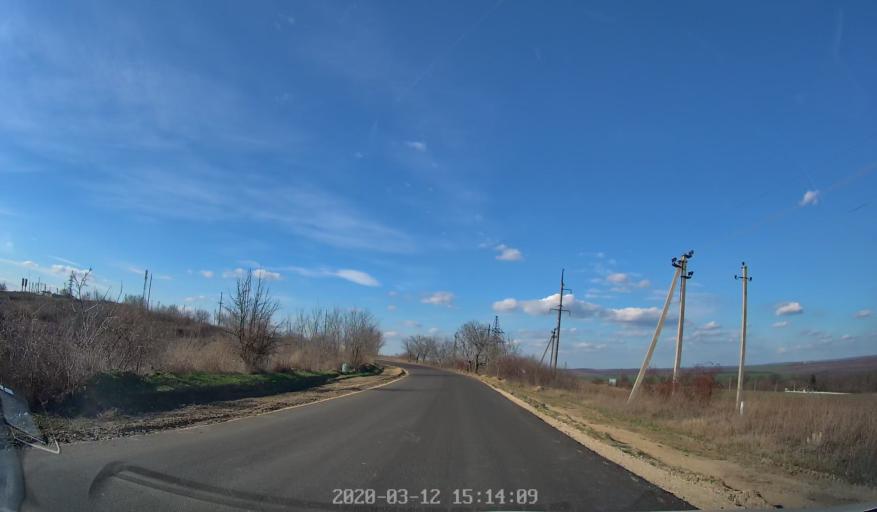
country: MD
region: Chisinau
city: Ciorescu
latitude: 47.2338
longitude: 28.9546
